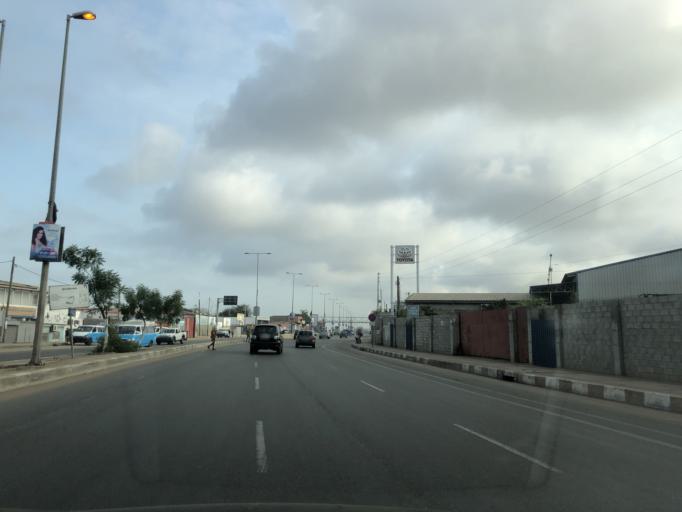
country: AO
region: Luanda
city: Luanda
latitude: -8.8732
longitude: 13.2113
